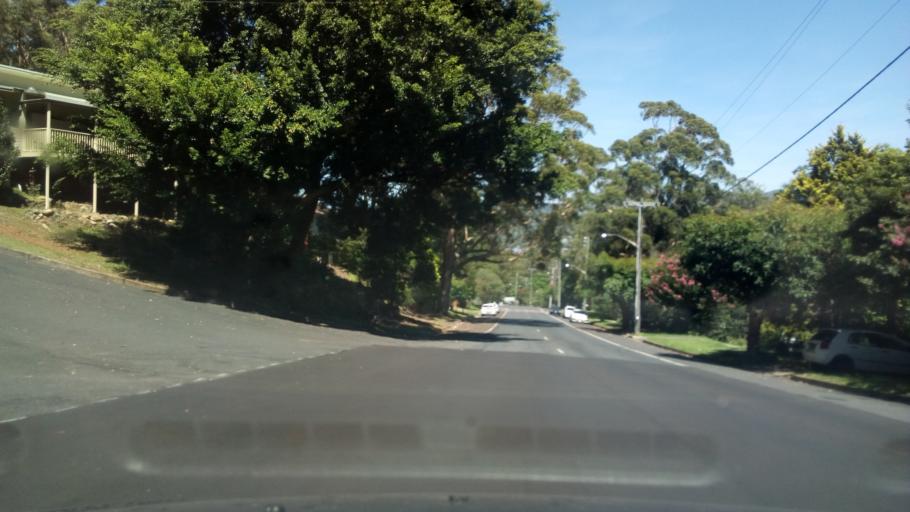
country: AU
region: New South Wales
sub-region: Wollongong
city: Mangerton
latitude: -34.4350
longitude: 150.8752
